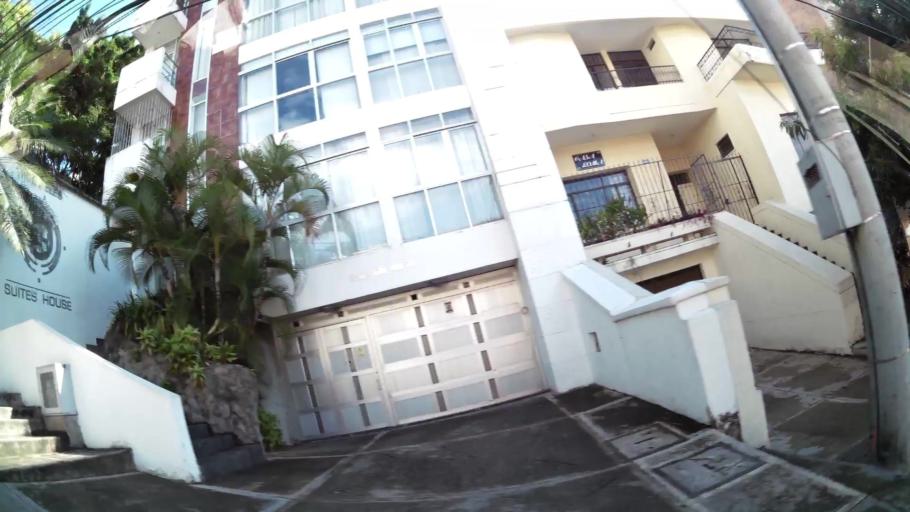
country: CO
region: Valle del Cauca
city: Cali
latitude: 3.4544
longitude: -76.5386
